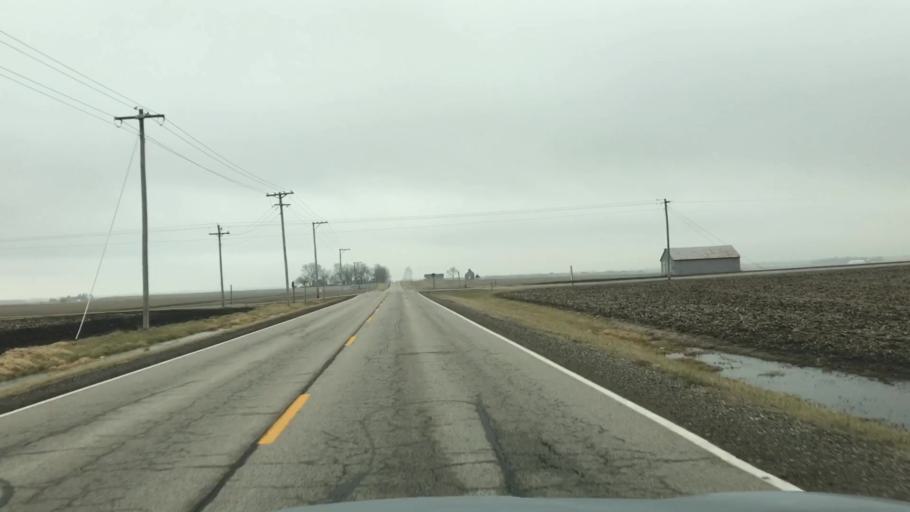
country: US
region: Illinois
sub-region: McLean County
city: Hudson
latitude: 40.5776
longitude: -88.9448
